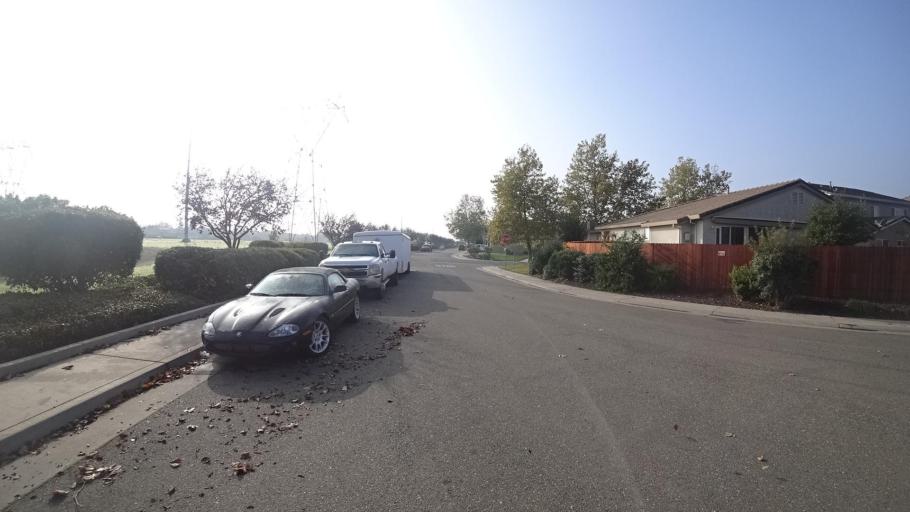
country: US
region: California
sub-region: Sacramento County
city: Elk Grove
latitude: 38.4077
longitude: -121.3510
